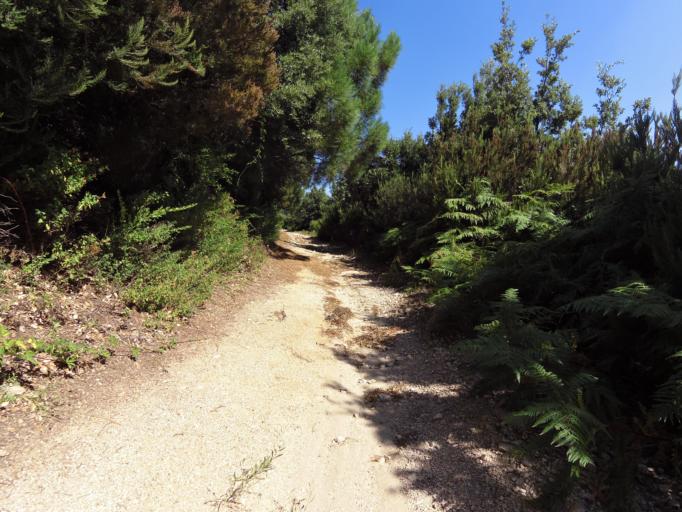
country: IT
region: Calabria
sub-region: Provincia di Reggio Calabria
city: Bivongi
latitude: 38.5095
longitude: 16.4351
